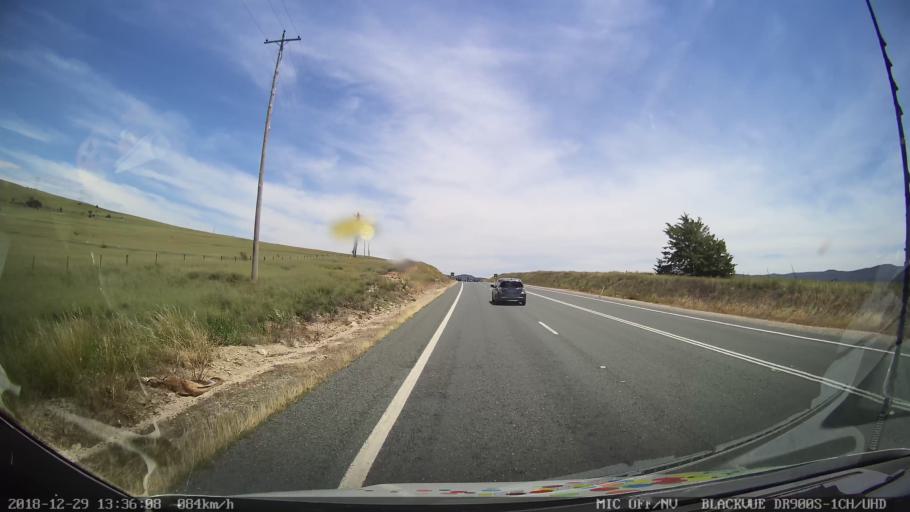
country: AU
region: New South Wales
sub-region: Cooma-Monaro
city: Cooma
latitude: -35.9670
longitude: 149.1439
